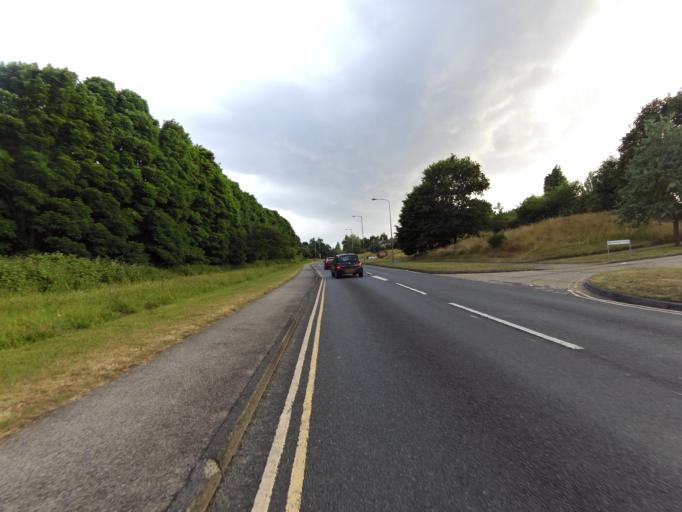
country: GB
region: England
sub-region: Suffolk
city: Ipswich
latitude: 52.0488
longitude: 1.1372
